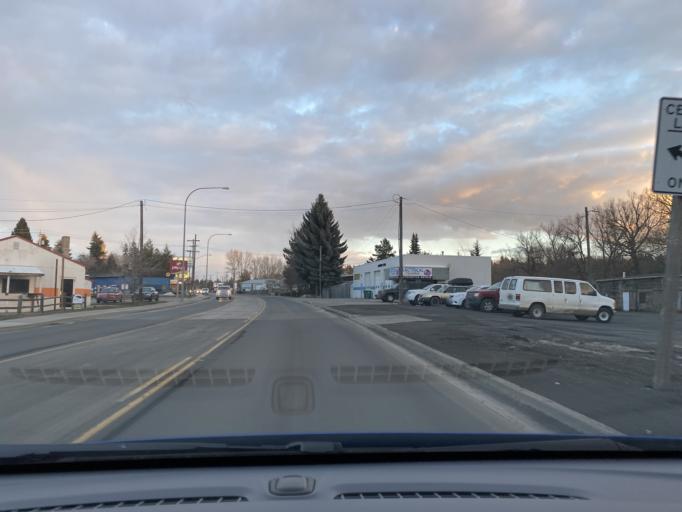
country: US
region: Idaho
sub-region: Latah County
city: Moscow
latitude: 46.7251
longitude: -116.9985
